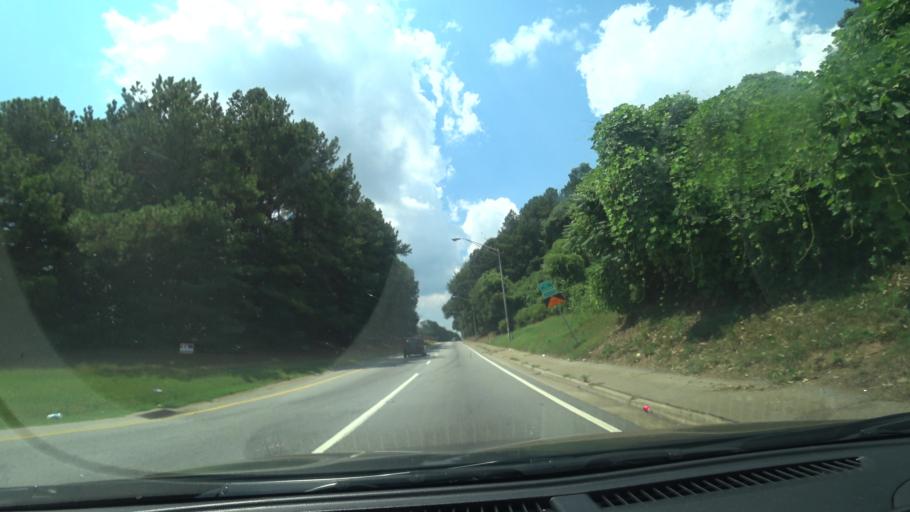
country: US
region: Georgia
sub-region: Fulton County
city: Hapeville
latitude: 33.6981
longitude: -84.3950
